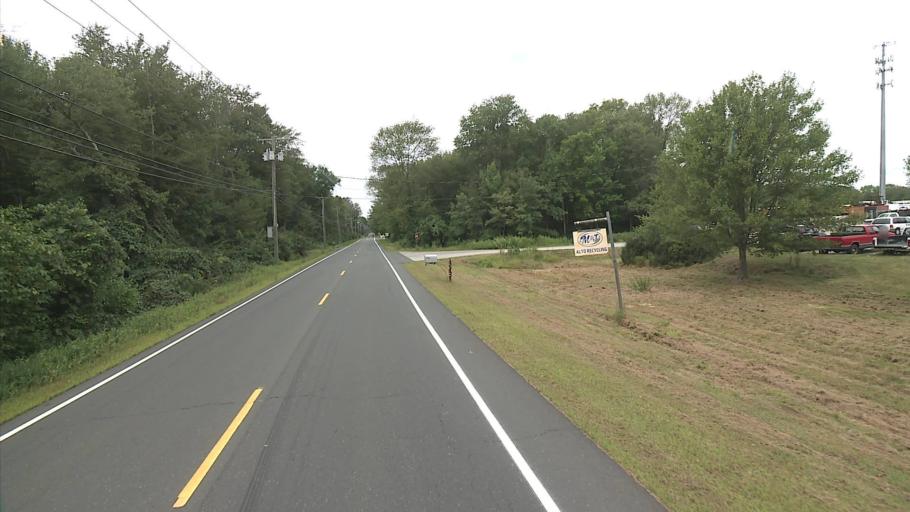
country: US
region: Connecticut
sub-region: New London County
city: Colchester
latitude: 41.5433
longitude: -72.3059
